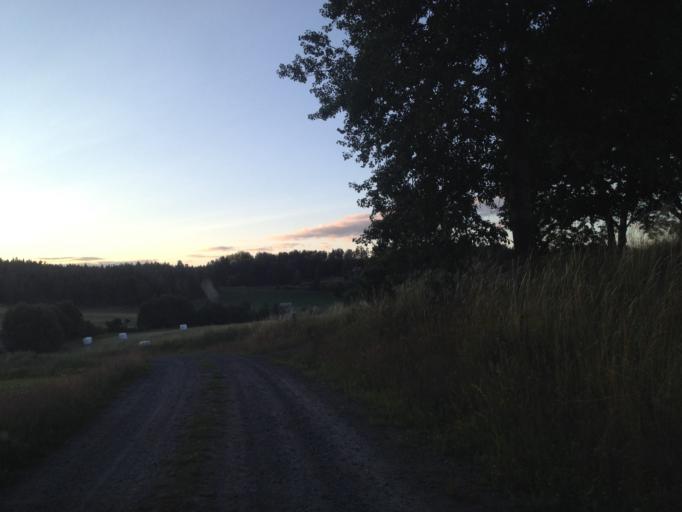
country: SE
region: Kalmar
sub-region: Vasterviks Kommun
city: Overum
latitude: 58.0194
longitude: 16.1206
